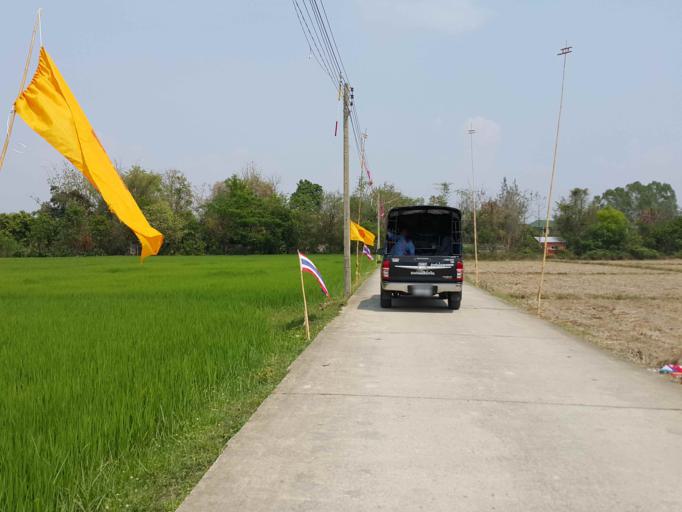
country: TH
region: Chiang Mai
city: San Kamphaeng
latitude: 18.7917
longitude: 99.0943
